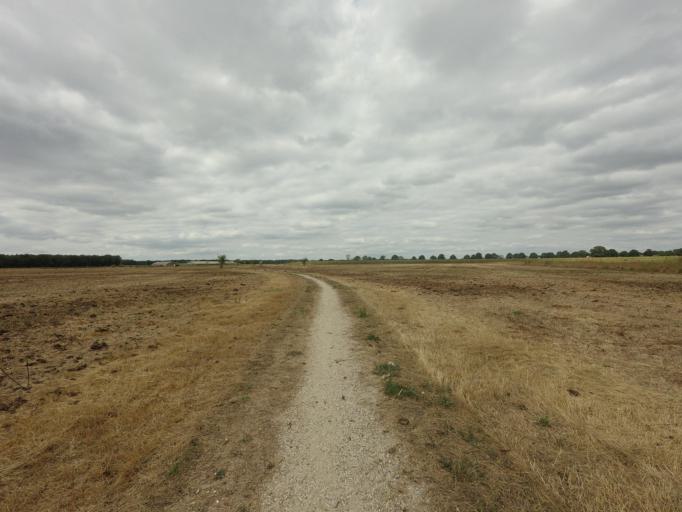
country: NL
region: North Brabant
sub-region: Gemeente Landerd
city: Zeeland
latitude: 51.7100
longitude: 5.6529
